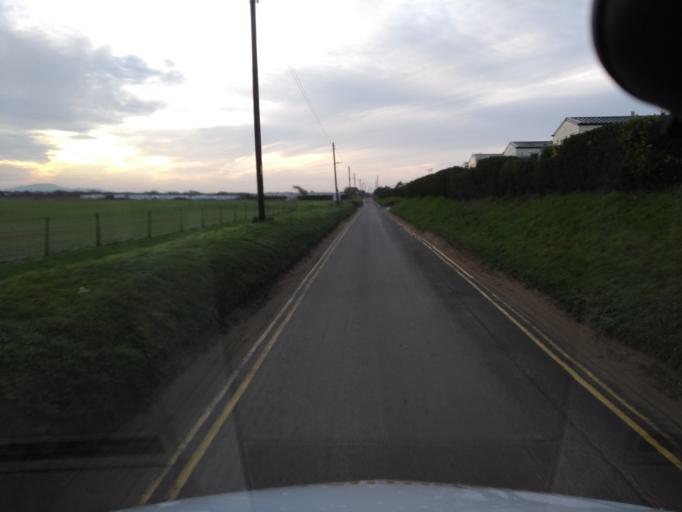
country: GB
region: England
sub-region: North Somerset
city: Weston-super-Mare
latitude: 51.3118
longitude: -3.0100
